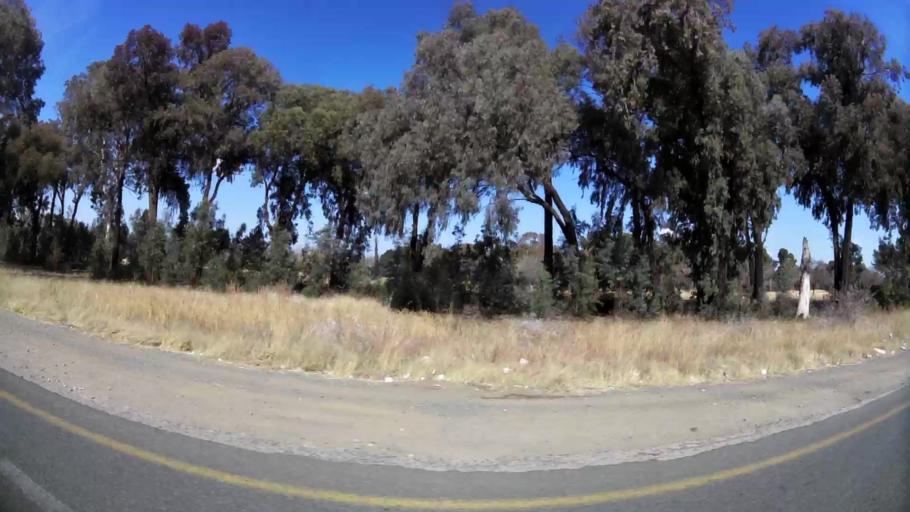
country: ZA
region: Orange Free State
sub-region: Mangaung Metropolitan Municipality
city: Bloemfontein
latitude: -29.1160
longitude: 26.2606
